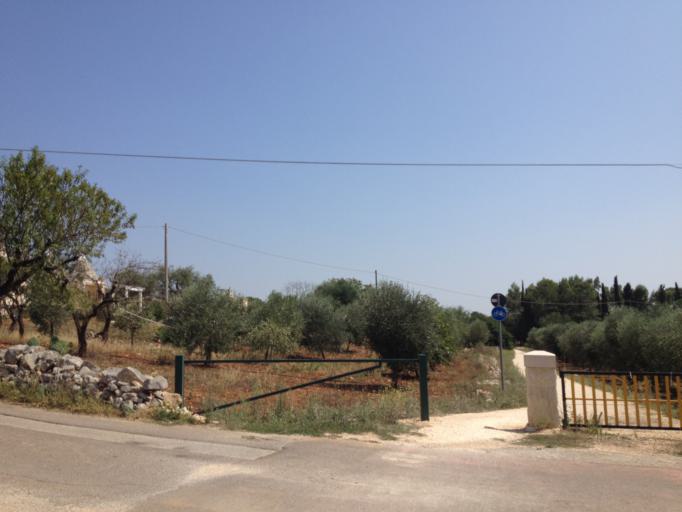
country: IT
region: Apulia
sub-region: Provincia di Brindisi
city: Cisternino
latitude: 40.7192
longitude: 17.4018
